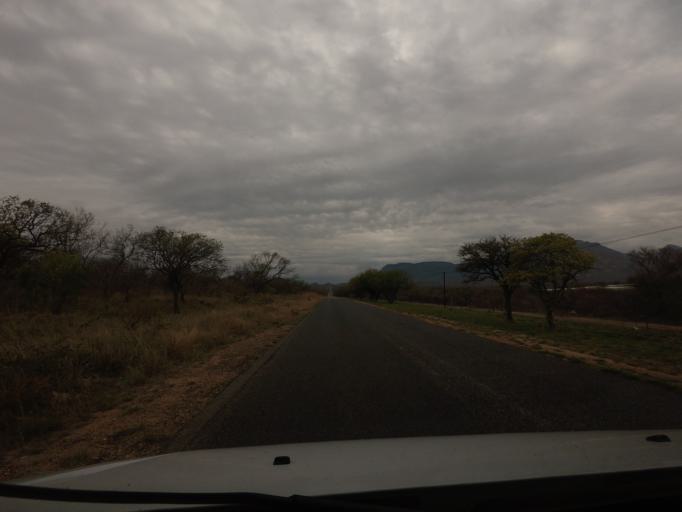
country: ZA
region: Limpopo
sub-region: Mopani District Municipality
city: Hoedspruit
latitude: -24.4634
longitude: 30.8718
